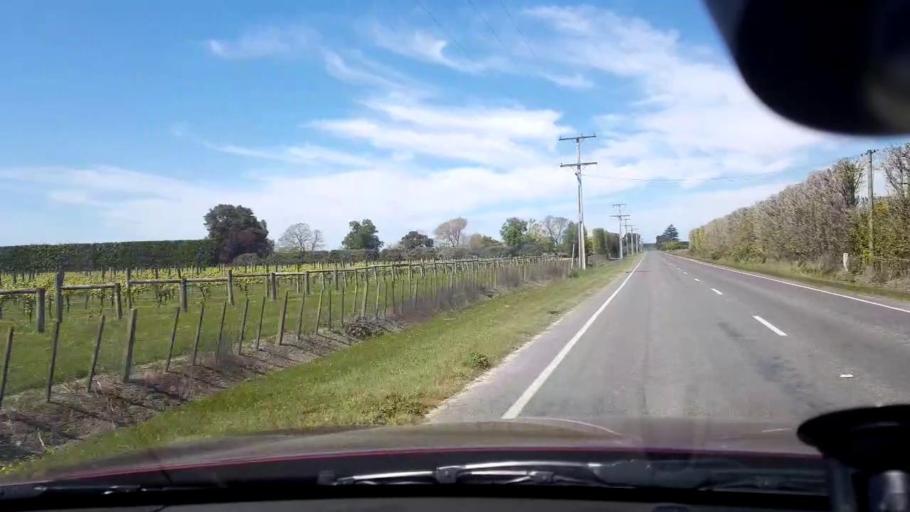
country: NZ
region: Gisborne
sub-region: Gisborne District
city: Gisborne
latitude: -38.6328
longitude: 177.9284
